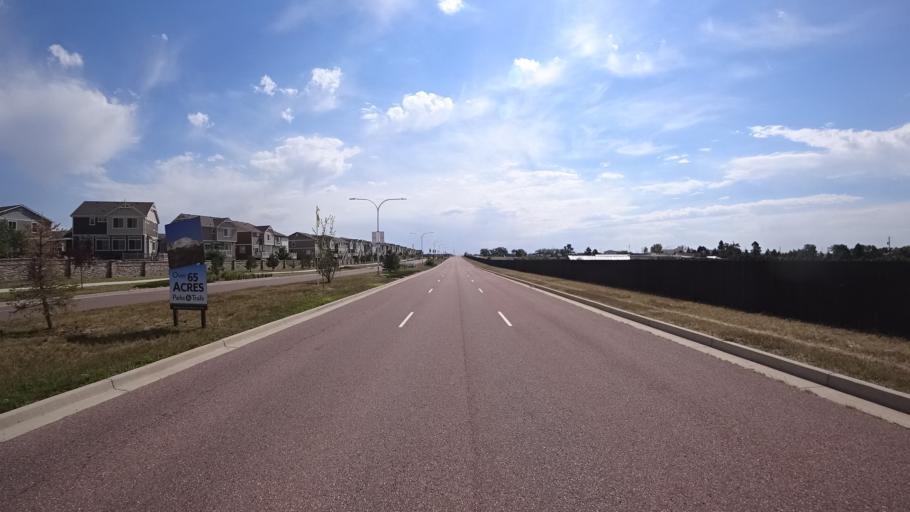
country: US
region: Colorado
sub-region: El Paso County
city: Cimarron Hills
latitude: 38.9265
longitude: -104.6756
